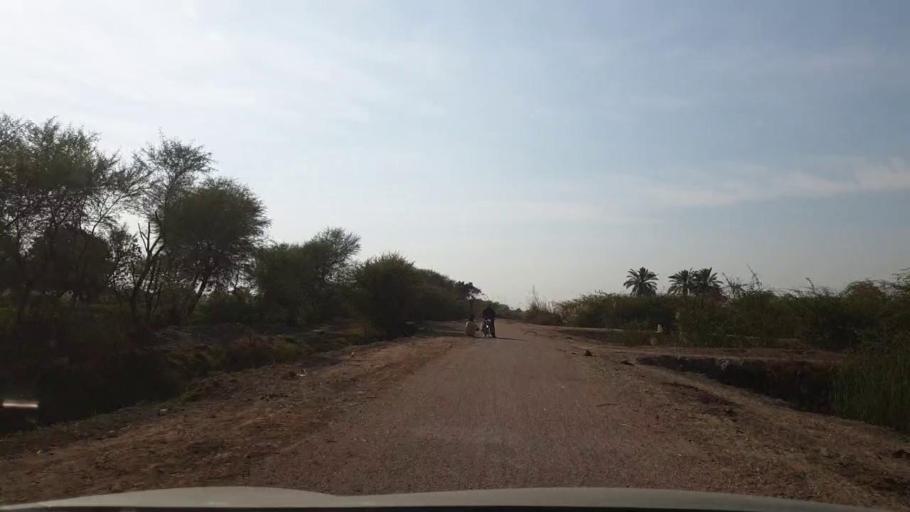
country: PK
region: Sindh
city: Berani
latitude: 25.7125
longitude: 68.8041
